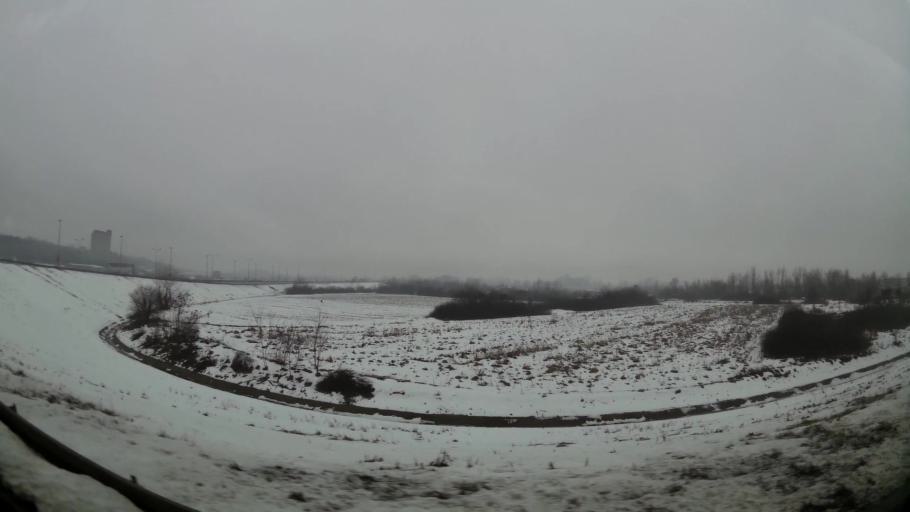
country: RS
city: Ostruznica
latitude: 44.7339
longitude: 20.3359
